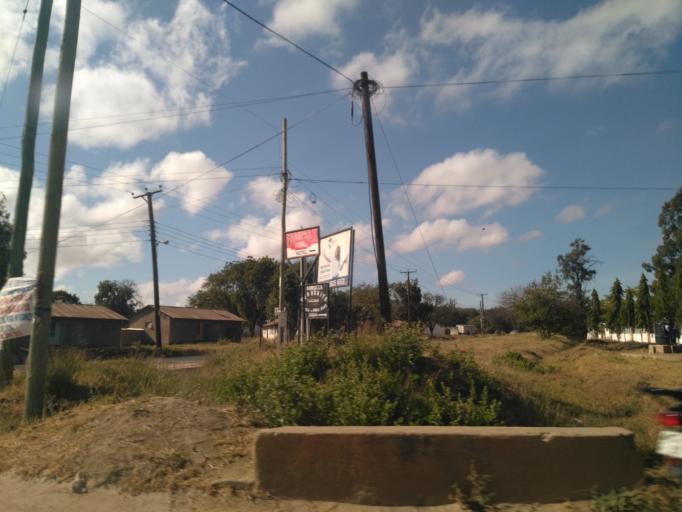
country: TZ
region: Dodoma
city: Dodoma
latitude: -6.1846
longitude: 35.7418
